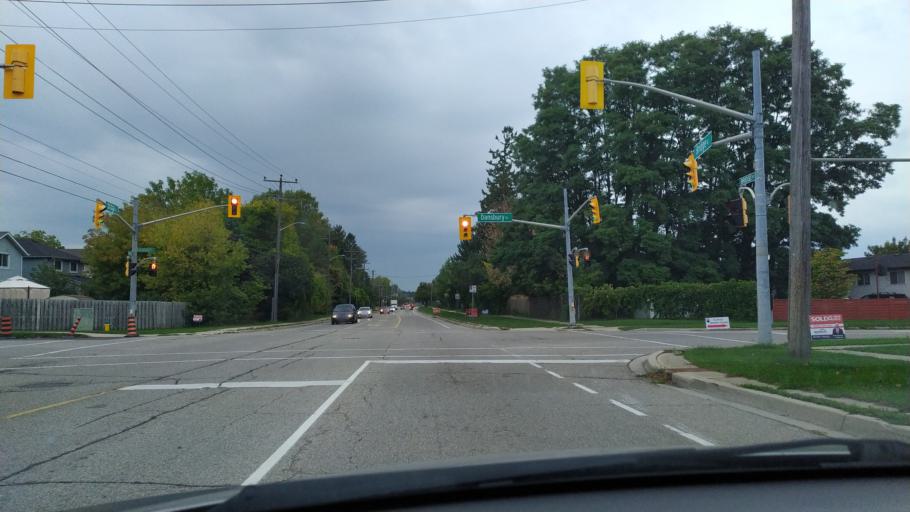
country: CA
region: Ontario
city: Waterloo
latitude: 43.4961
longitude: -80.5013
